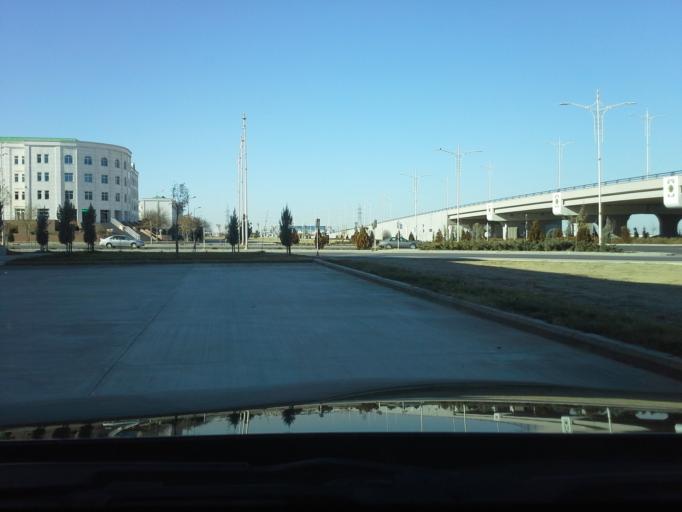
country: TM
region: Ahal
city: Ashgabat
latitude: 37.9769
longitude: 58.3425
